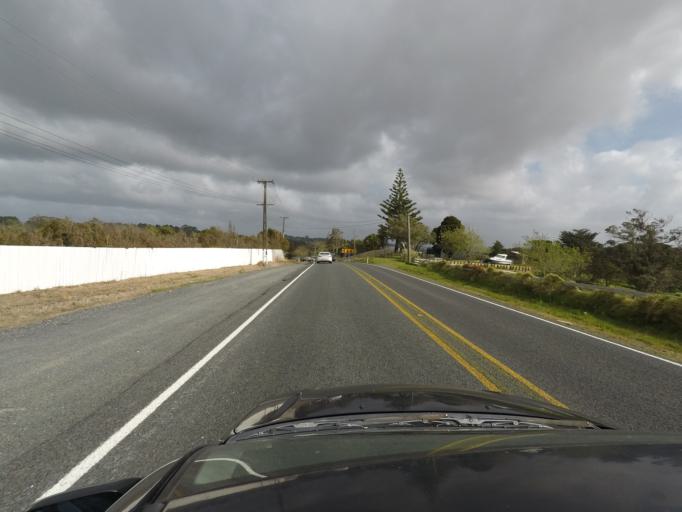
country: NZ
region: Auckland
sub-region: Auckland
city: Pakuranga
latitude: -36.9328
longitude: 174.9379
